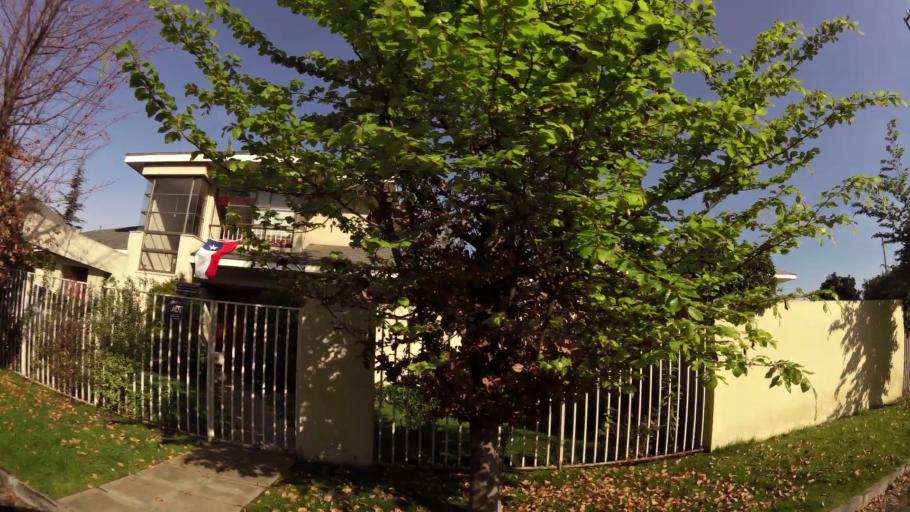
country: CL
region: Santiago Metropolitan
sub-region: Provincia de Santiago
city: Villa Presidente Frei, Nunoa, Santiago, Chile
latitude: -33.4912
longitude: -70.5520
